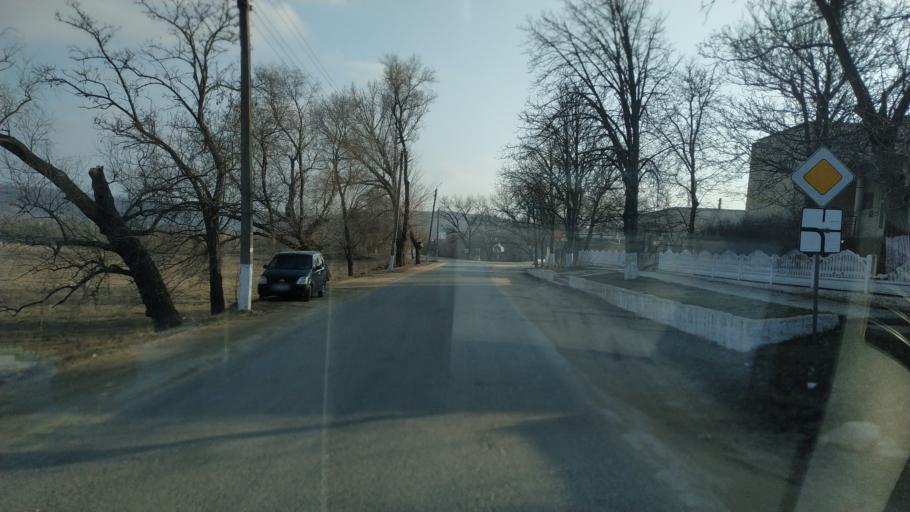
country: MD
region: Hincesti
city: Dancu
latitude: 46.7664
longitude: 28.3458
